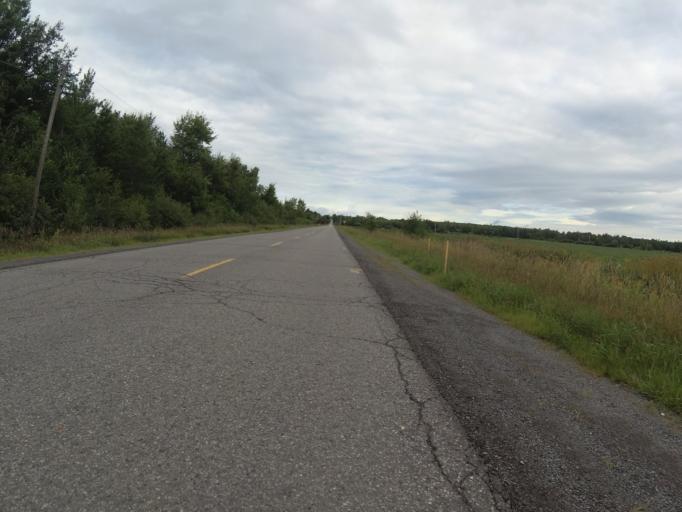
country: CA
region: Ontario
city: Clarence-Rockland
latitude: 45.4164
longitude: -75.2924
